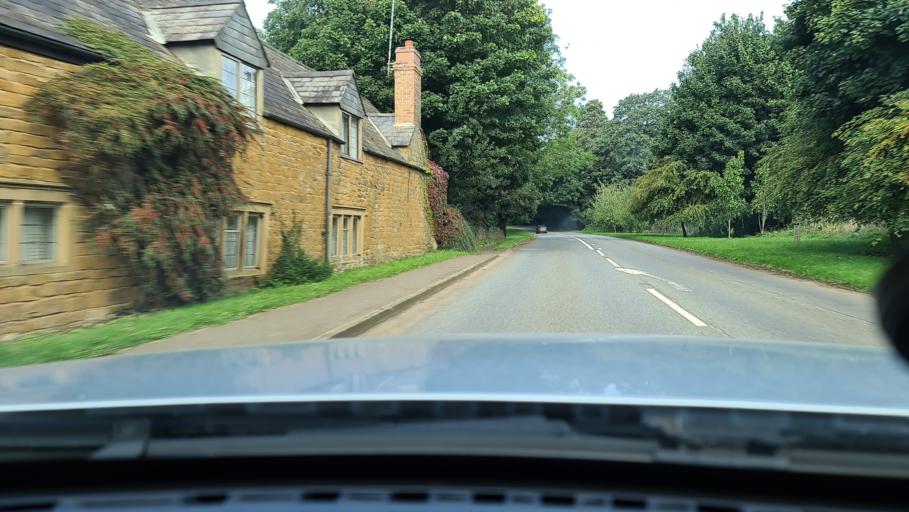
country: GB
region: England
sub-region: Oxfordshire
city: Hanwell
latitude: 52.0739
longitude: -1.3956
